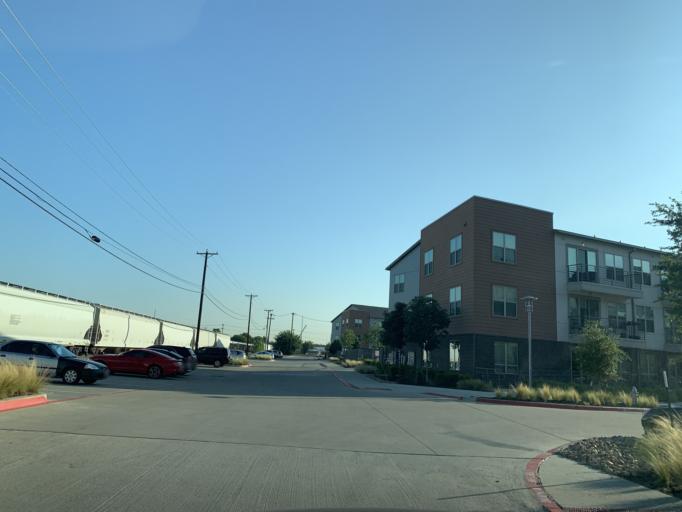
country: US
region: Texas
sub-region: Tarrant County
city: Fort Worth
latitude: 32.7540
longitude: -97.3507
